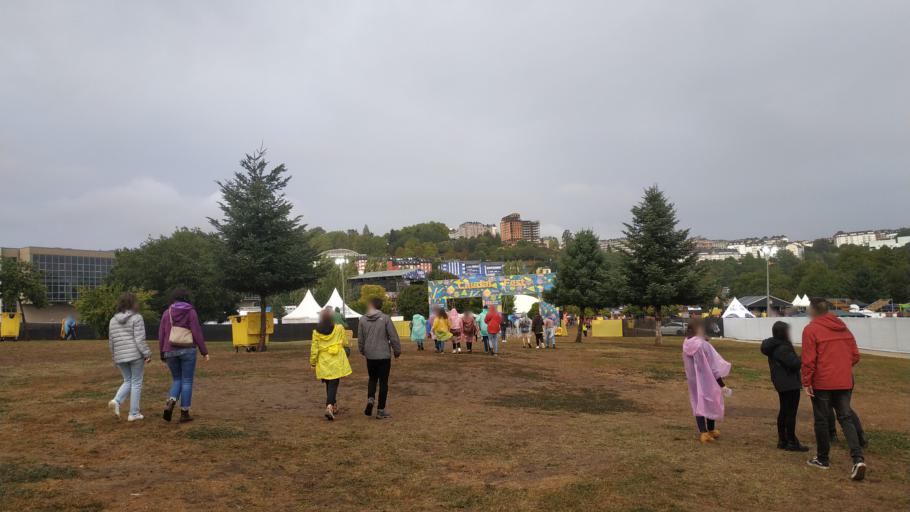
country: ES
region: Galicia
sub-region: Provincia de Lugo
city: Lugo
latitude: 43.0022
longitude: -7.5688
